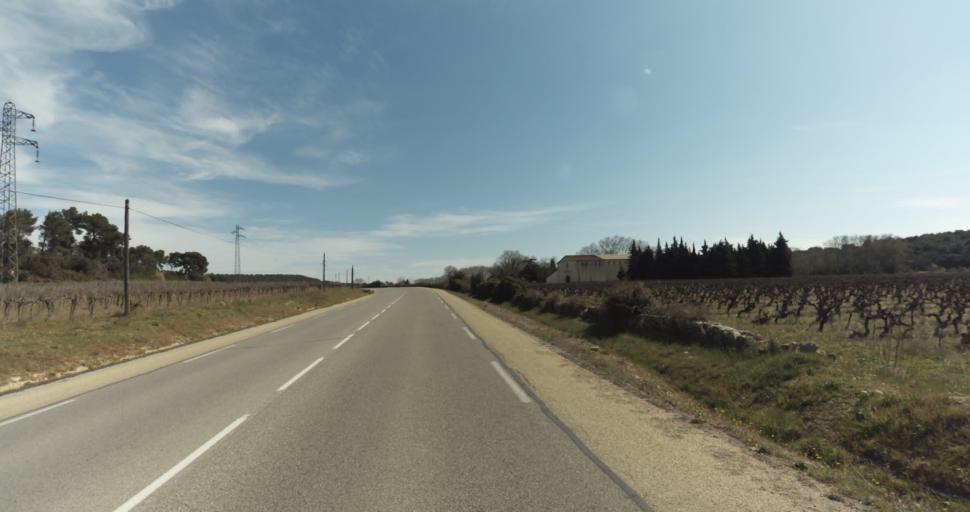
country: FR
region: Provence-Alpes-Cote d'Azur
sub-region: Departement des Bouches-du-Rhone
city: Lambesc
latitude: 43.6480
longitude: 5.2120
